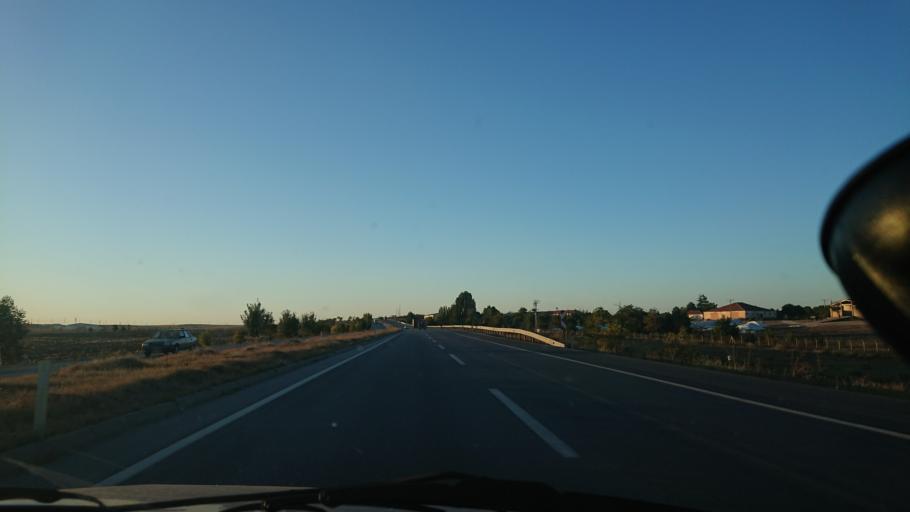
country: TR
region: Eskisehir
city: Mahmudiye
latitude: 39.4788
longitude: 30.9900
